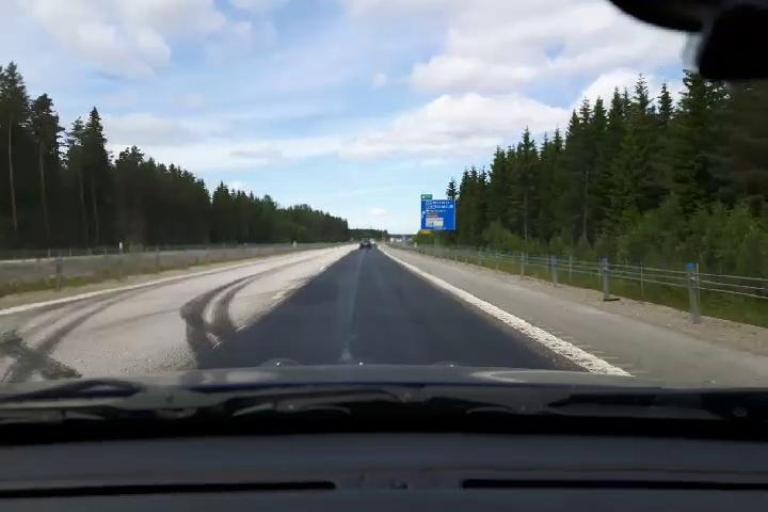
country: SE
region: Uppsala
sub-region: Alvkarleby Kommun
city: AElvkarleby
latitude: 60.4486
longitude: 17.4165
